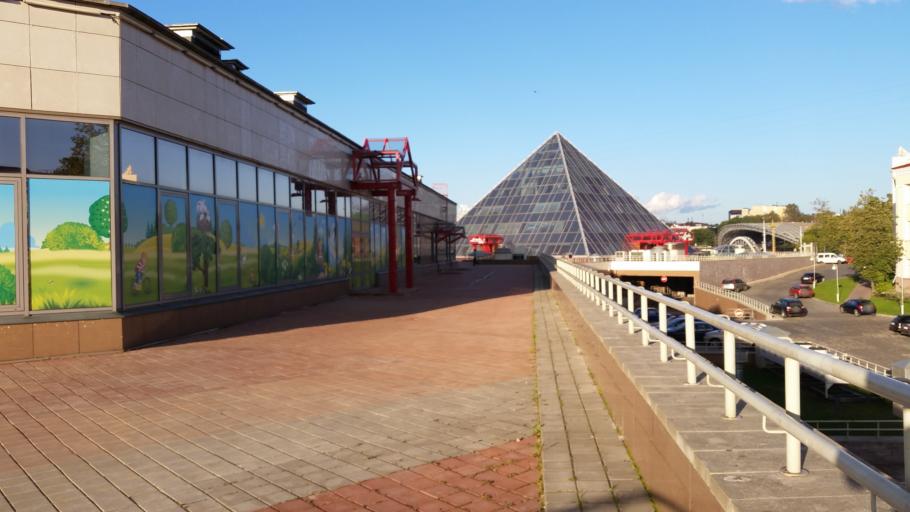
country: BY
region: Vitebsk
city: Vitebsk
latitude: 55.1907
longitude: 30.2028
